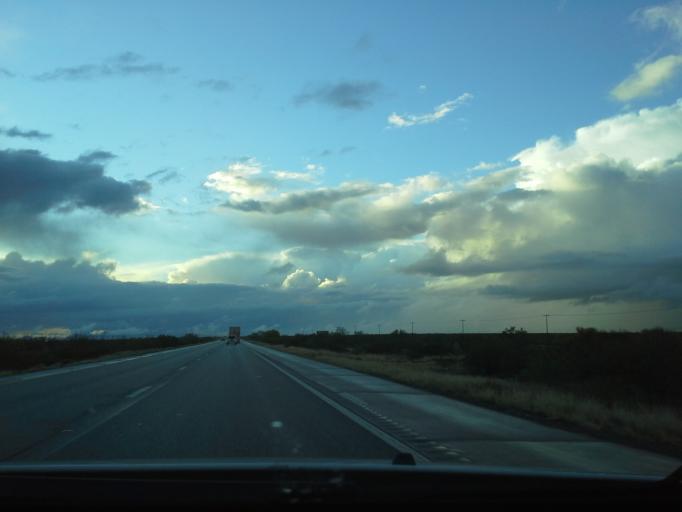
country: US
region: Arizona
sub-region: Pima County
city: Vail
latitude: 32.0345
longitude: -110.7289
